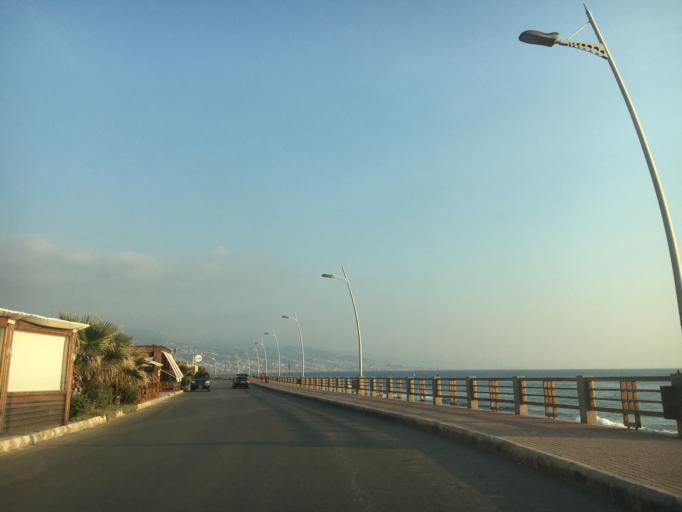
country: LB
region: Mont-Liban
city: Jbail
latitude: 34.1441
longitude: 35.6277
